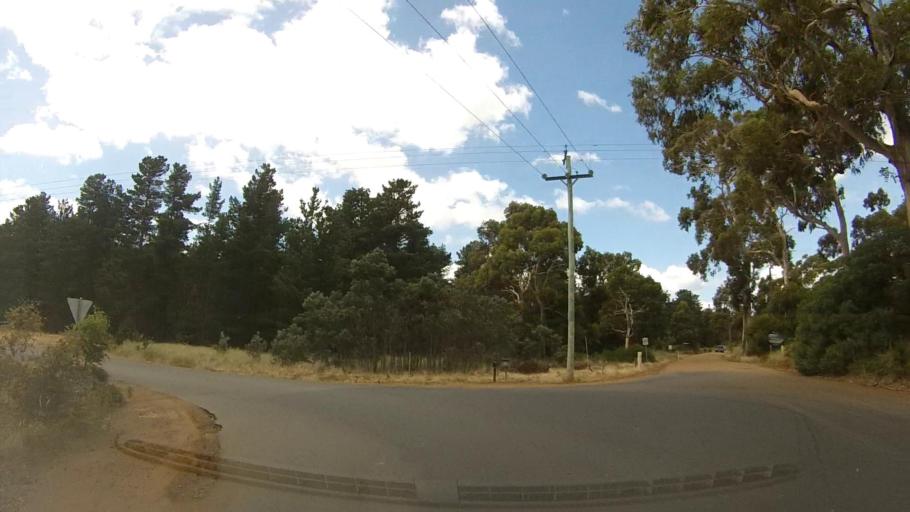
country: AU
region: Tasmania
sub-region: Clarence
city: Seven Mile Beach
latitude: -42.8430
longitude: 147.5336
